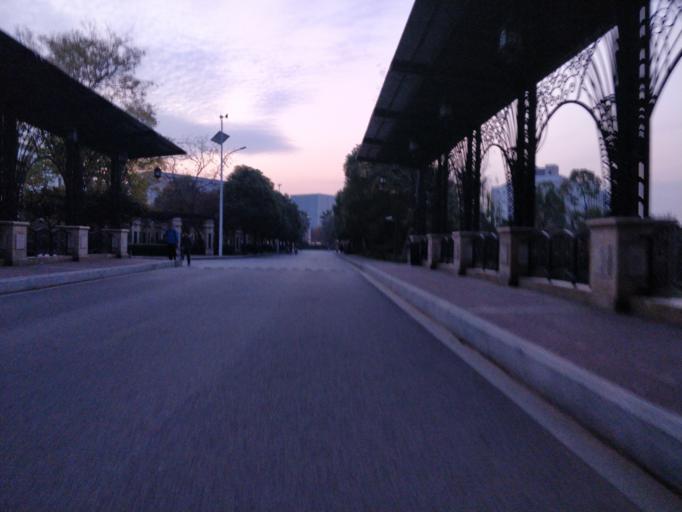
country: CN
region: Shanghai Shi
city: Huangdu
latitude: 31.2895
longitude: 121.2153
